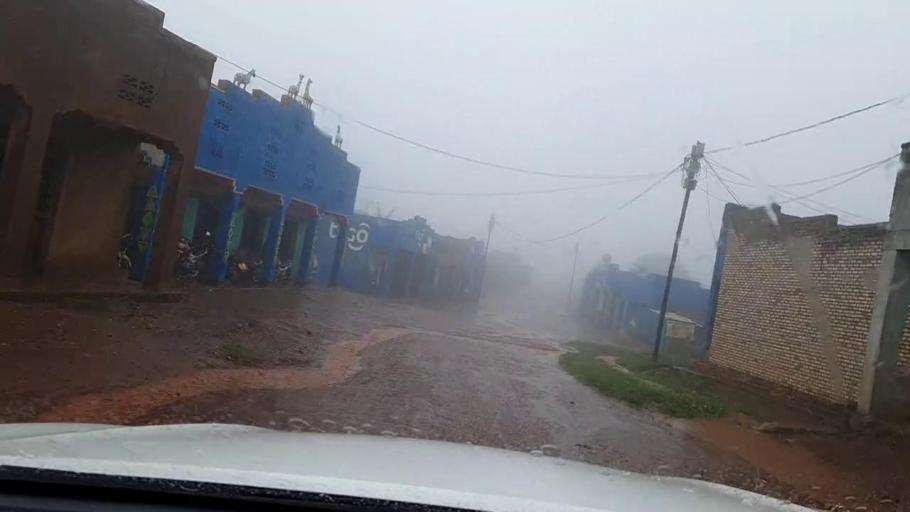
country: RW
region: Northern Province
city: Byumba
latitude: -1.7318
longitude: 30.0184
